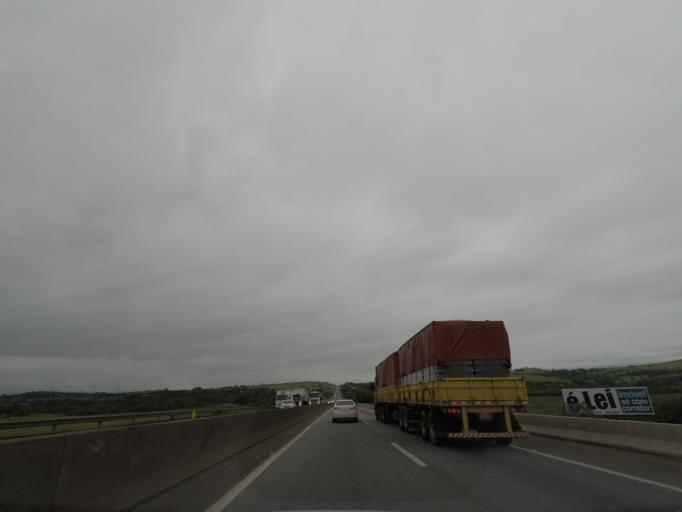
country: BR
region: Sao Paulo
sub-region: Taubate
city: Taubate
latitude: -23.0020
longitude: -45.5036
